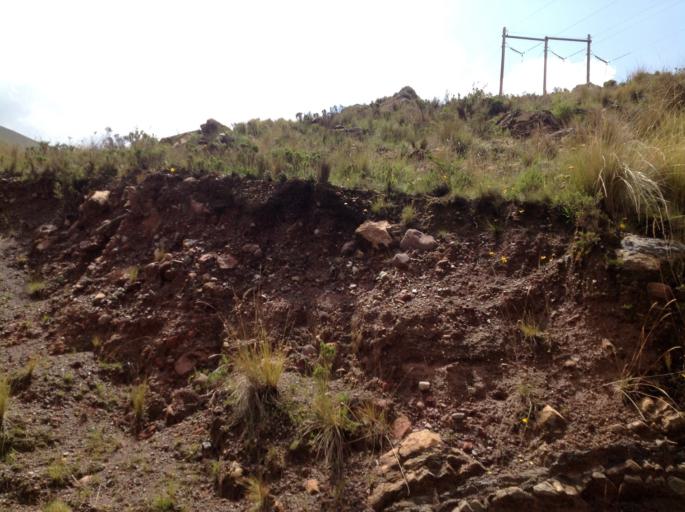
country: BO
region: La Paz
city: Yumani
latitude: -15.7727
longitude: -69.0054
